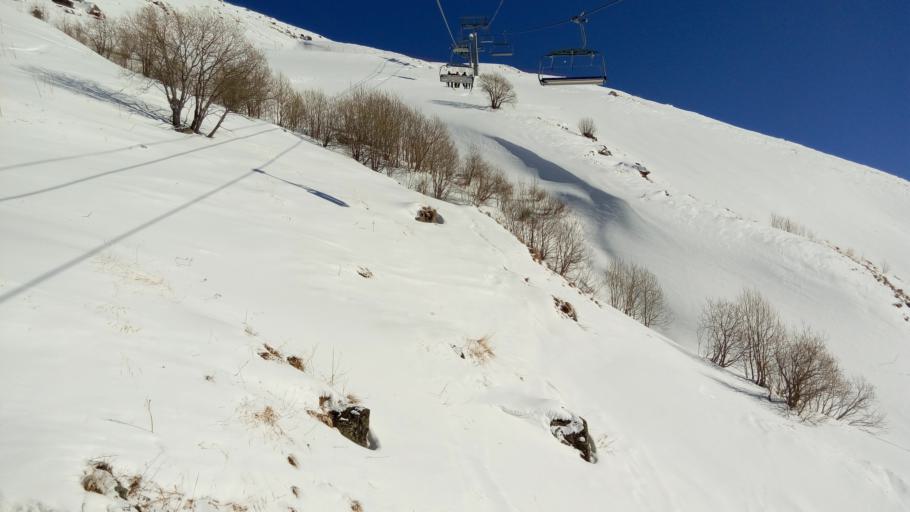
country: RU
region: Karachayevo-Cherkesiya
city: Teberda
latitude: 43.2913
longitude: 41.6549
